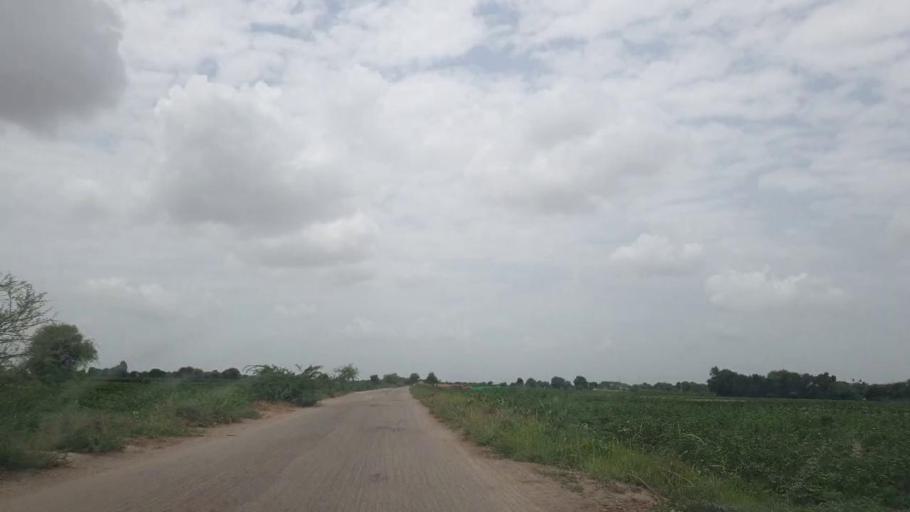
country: PK
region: Sindh
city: Naukot
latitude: 24.9127
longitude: 69.2689
